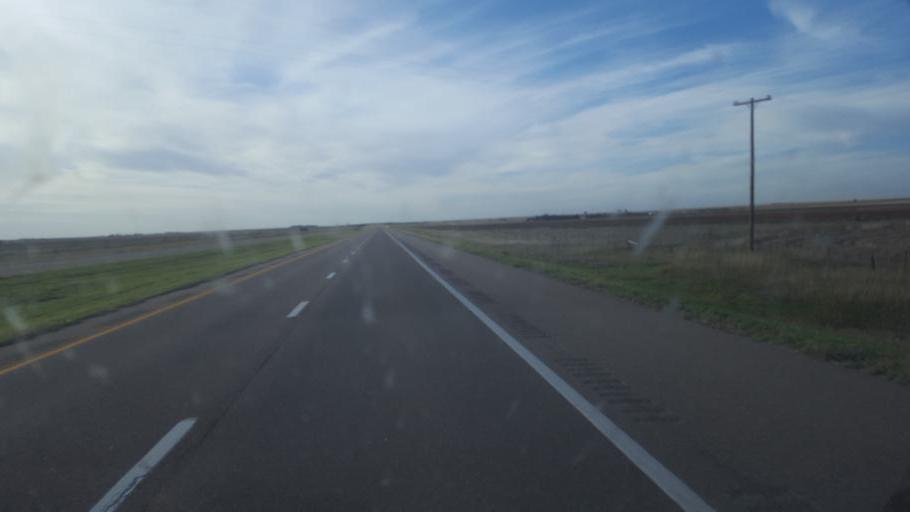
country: US
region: Kansas
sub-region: Gove County
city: Gove
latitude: 39.0664
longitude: -100.2593
